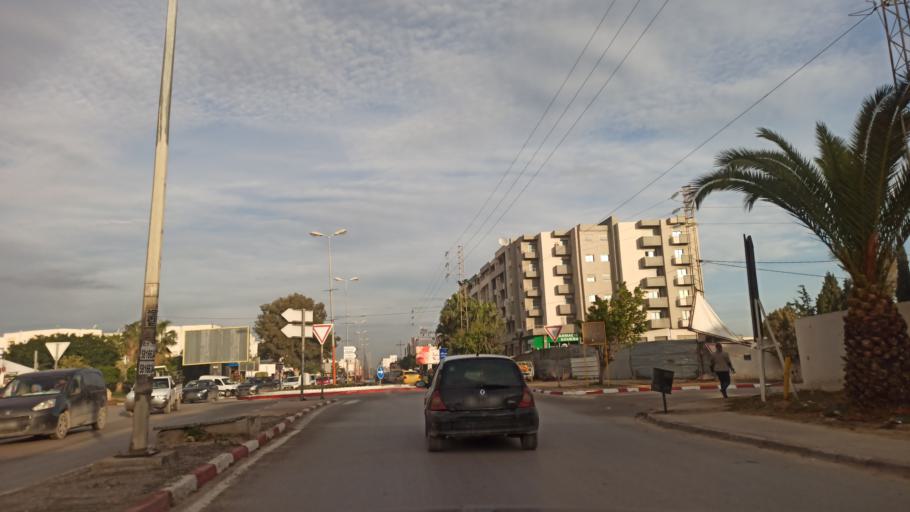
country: TN
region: Ariana
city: Ariana
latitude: 36.8614
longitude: 10.2546
